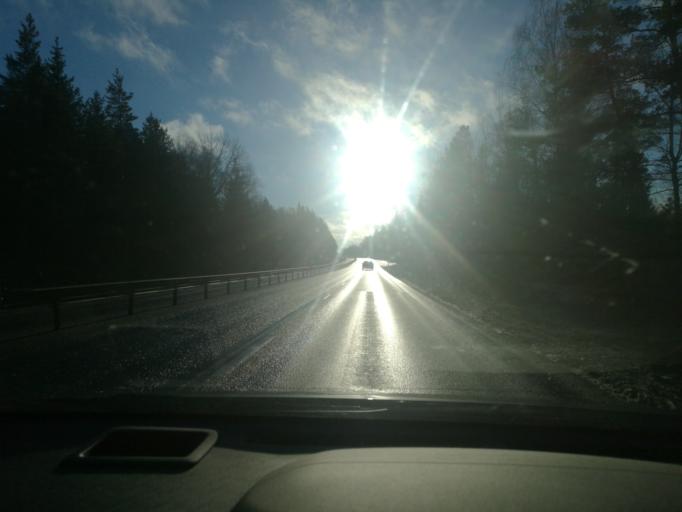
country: SE
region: OEstergoetland
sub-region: Norrkopings Kommun
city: Jursla
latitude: 58.7180
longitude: 16.1663
